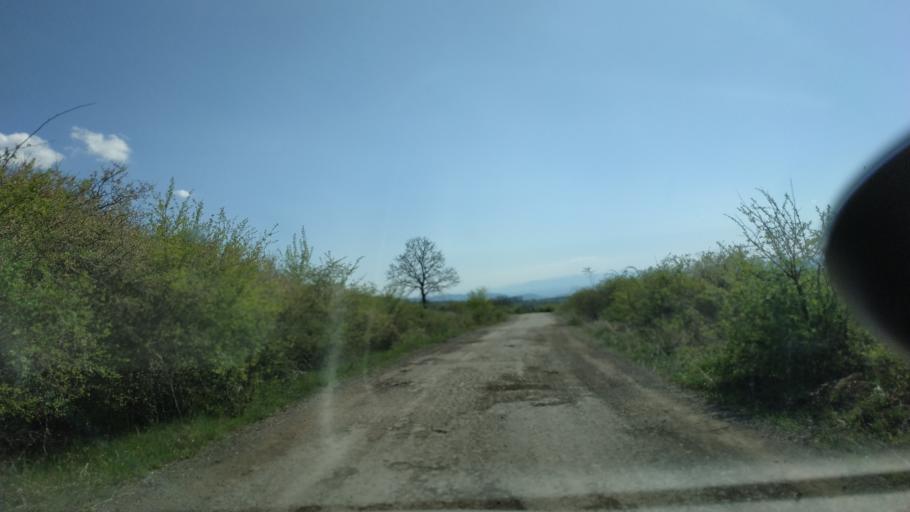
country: RS
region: Central Serbia
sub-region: Zajecarski Okrug
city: Soko Banja
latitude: 43.5234
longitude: 21.9055
